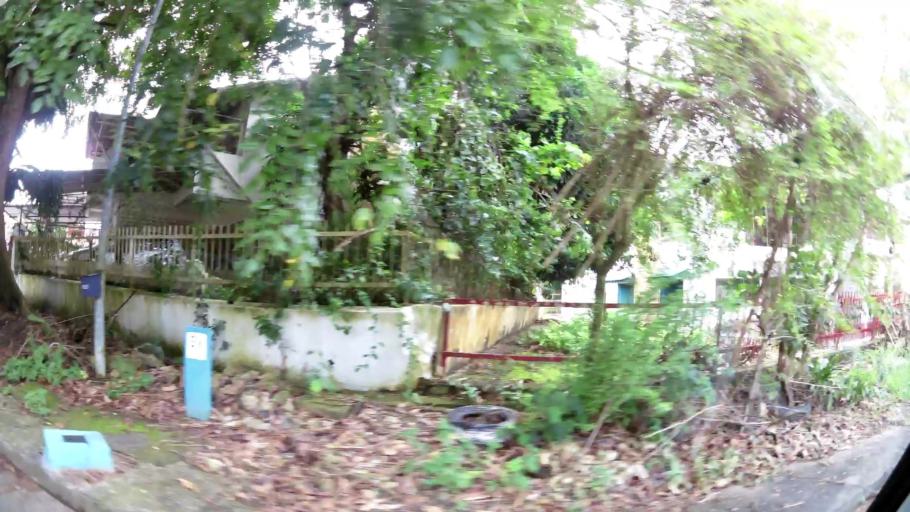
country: BN
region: Brunei and Muara
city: Bandar Seri Begawan
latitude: 4.8858
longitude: 114.9236
